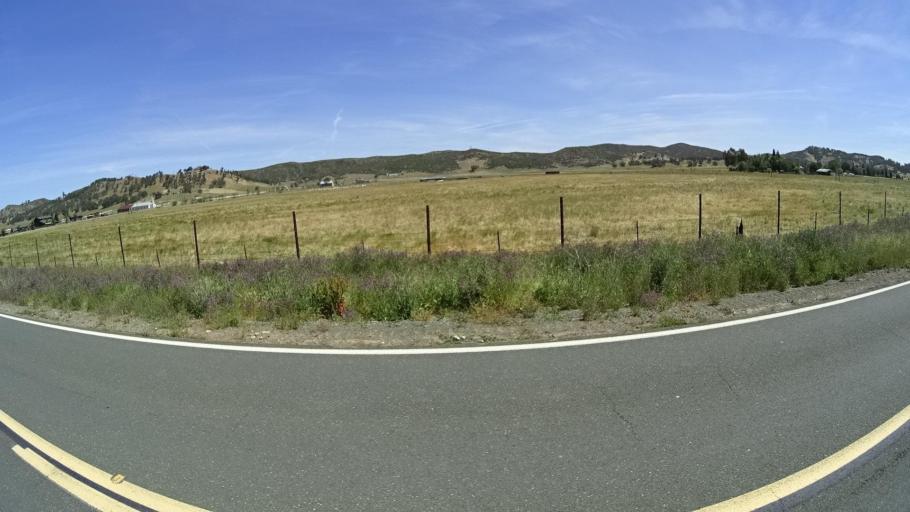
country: US
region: California
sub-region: Lake County
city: Middletown
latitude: 38.7456
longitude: -122.5774
